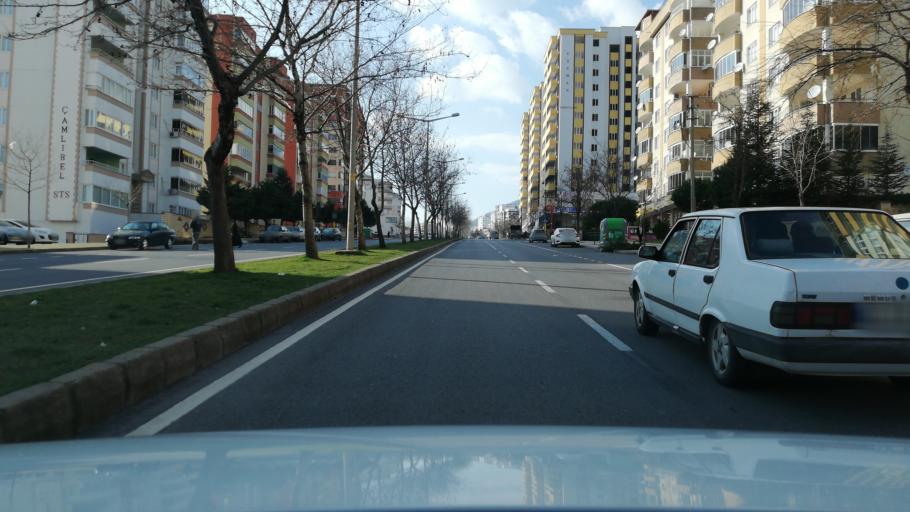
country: TR
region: Kahramanmaras
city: Kahramanmaras
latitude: 37.5936
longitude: 36.8959
